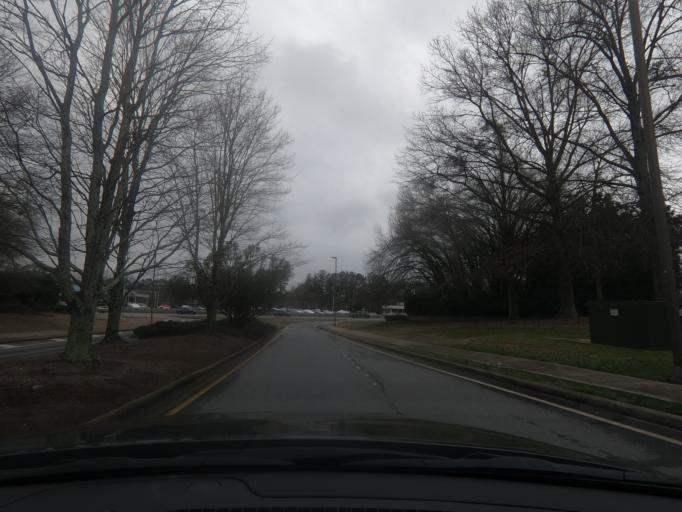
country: US
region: Georgia
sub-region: Cobb County
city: Kennesaw
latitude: 34.0030
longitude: -84.5966
